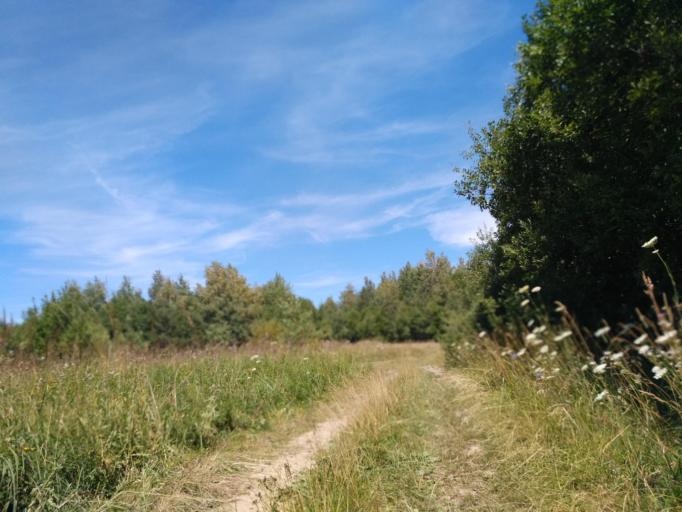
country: PL
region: Subcarpathian Voivodeship
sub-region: Powiat sanocki
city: Bukowsko
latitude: 49.4793
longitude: 22.0916
